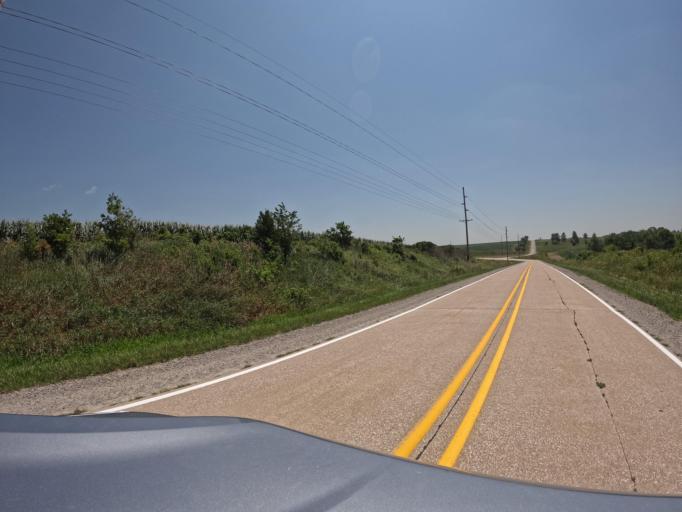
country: US
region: Iowa
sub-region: Keokuk County
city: Sigourney
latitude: 41.2785
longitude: -92.1807
